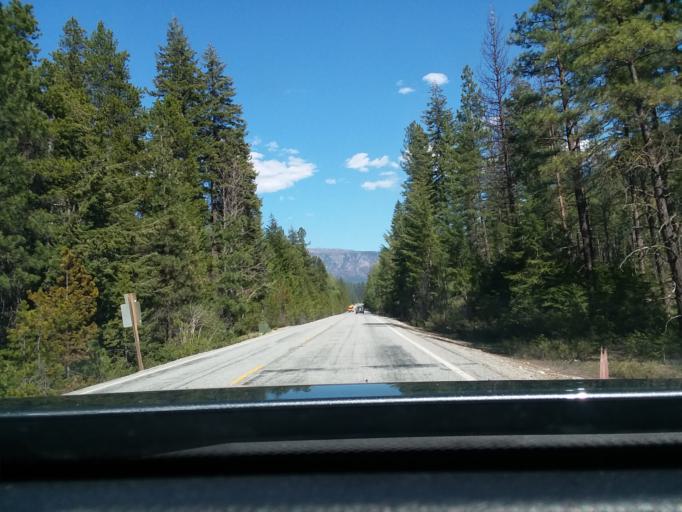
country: US
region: Washington
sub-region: Chelan County
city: Leavenworth
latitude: 47.8036
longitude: -120.7062
